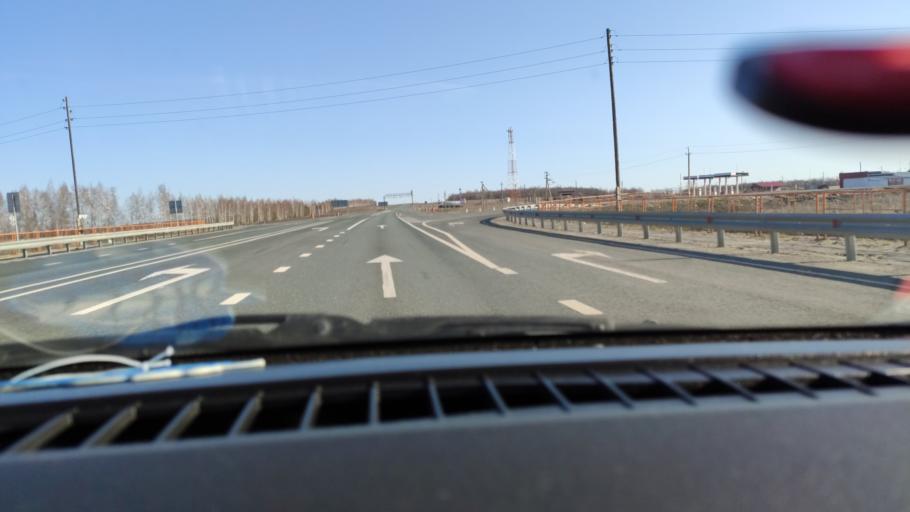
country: RU
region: Samara
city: Syzran'
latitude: 52.9251
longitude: 48.3038
